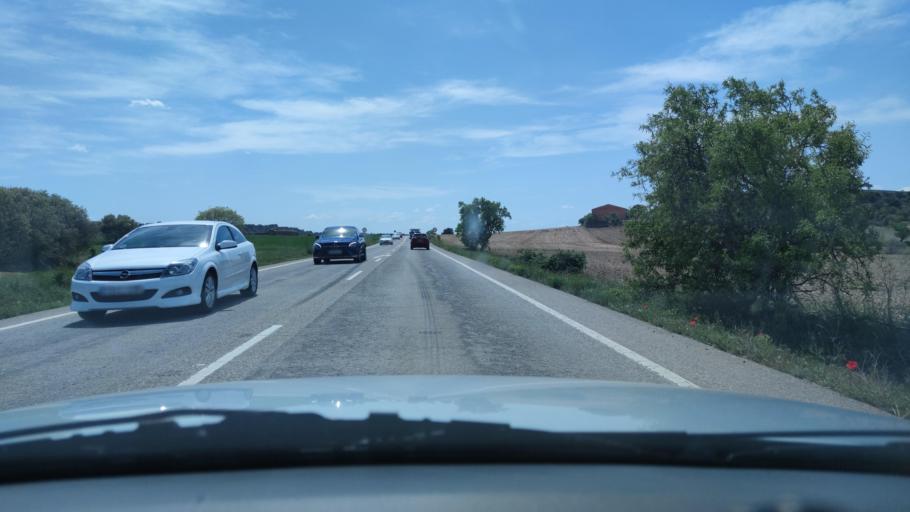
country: ES
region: Catalonia
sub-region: Provincia de Lleida
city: Mont-roig del Camp
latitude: 41.6996
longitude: 1.1773
